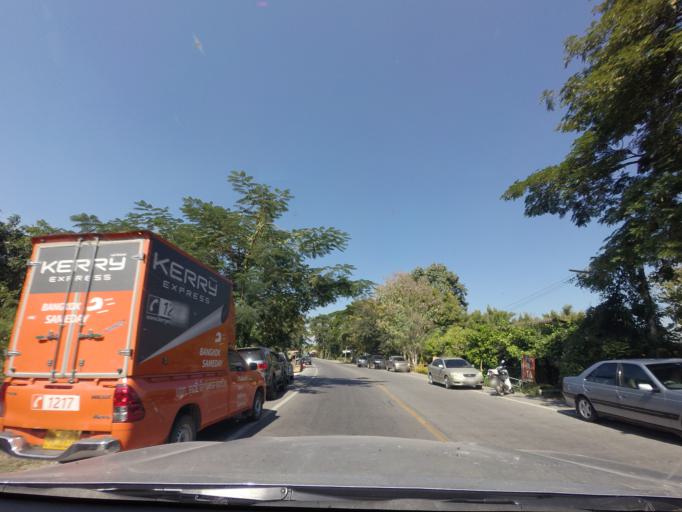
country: TH
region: Chiang Mai
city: San Sai
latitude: 18.9194
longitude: 98.9409
